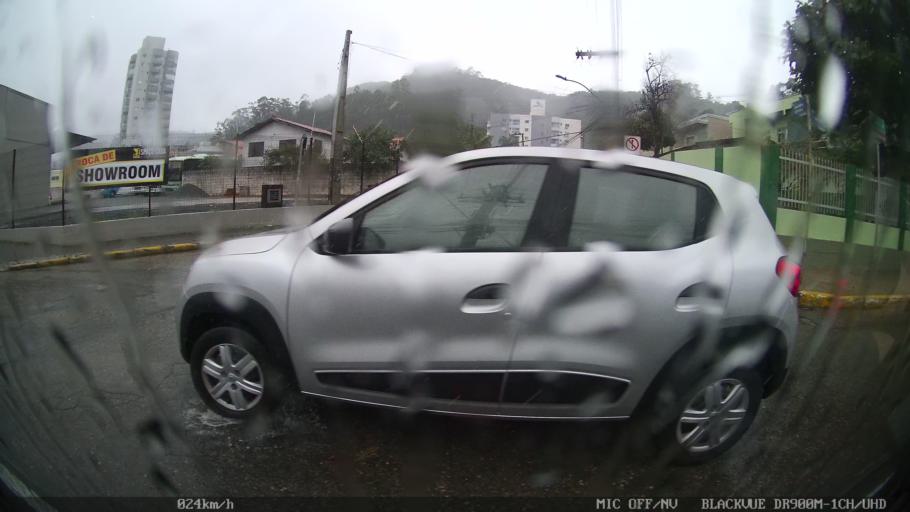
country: BR
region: Santa Catarina
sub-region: Itajai
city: Itajai
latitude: -26.9316
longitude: -48.6433
